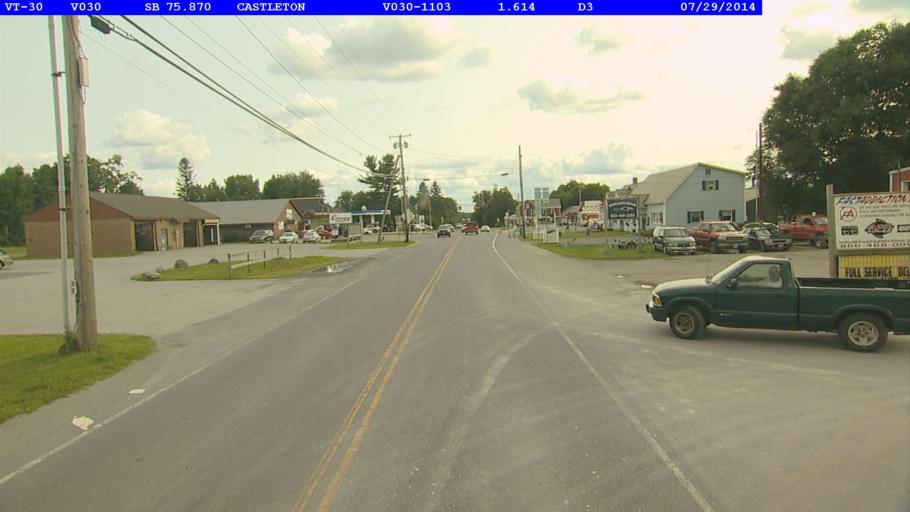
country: US
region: Vermont
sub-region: Rutland County
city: Castleton
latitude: 43.6099
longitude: -73.2081
